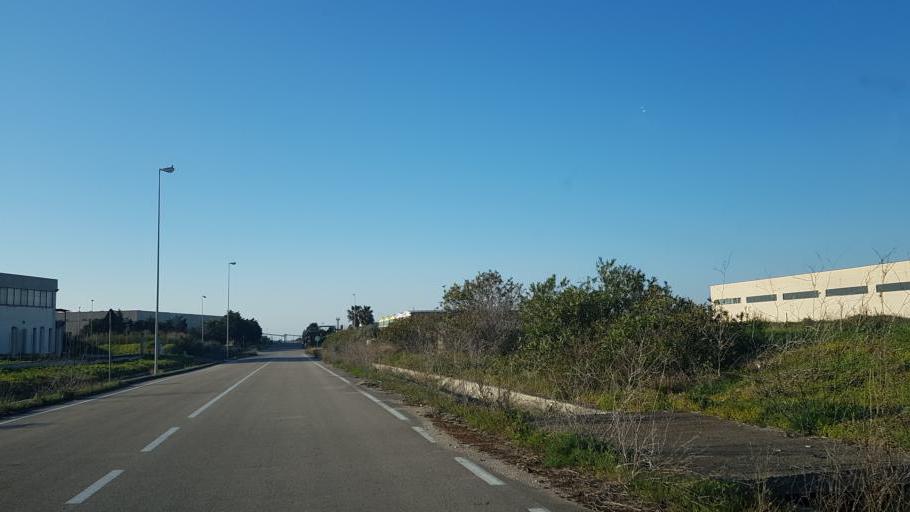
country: IT
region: Apulia
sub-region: Provincia di Brindisi
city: La Rosa
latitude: 40.6242
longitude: 17.9707
